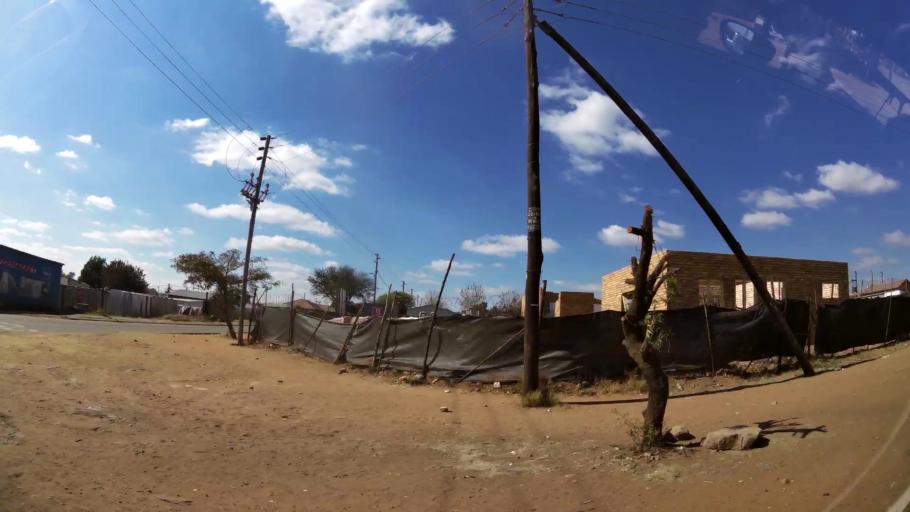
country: ZA
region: Gauteng
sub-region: West Rand District Municipality
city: Krugersdorp
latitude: -26.1441
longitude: 27.7851
